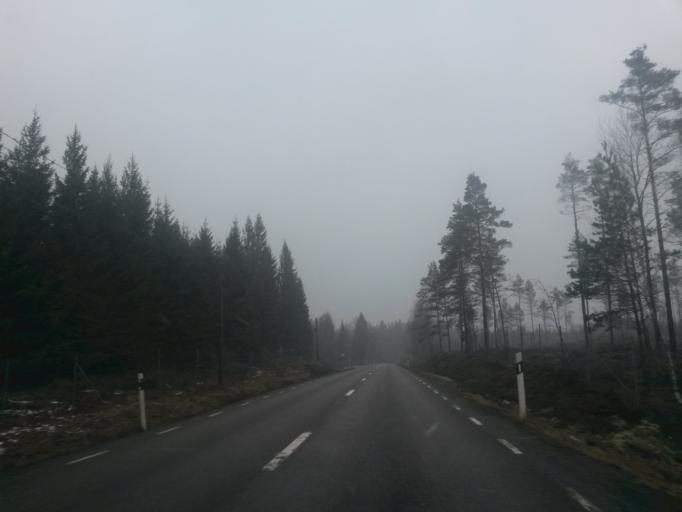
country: SE
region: Vaestra Goetaland
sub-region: Alingsas Kommun
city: Sollebrunn
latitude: 58.1991
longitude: 12.4309
